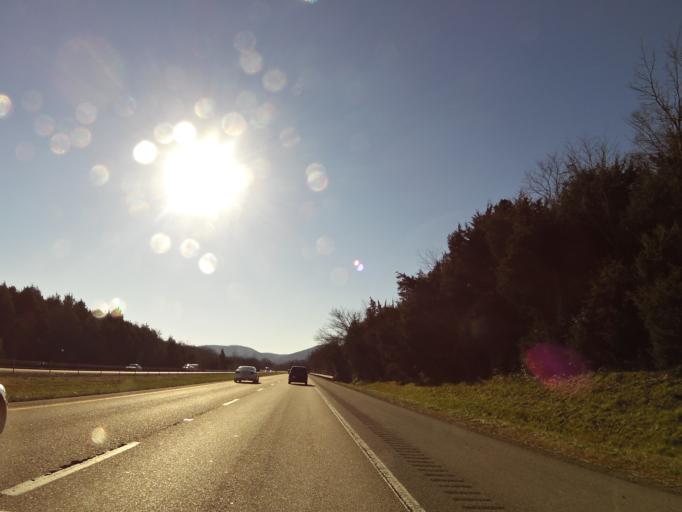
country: US
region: Tennessee
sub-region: Cocke County
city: Newport
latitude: 35.9932
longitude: -83.2858
